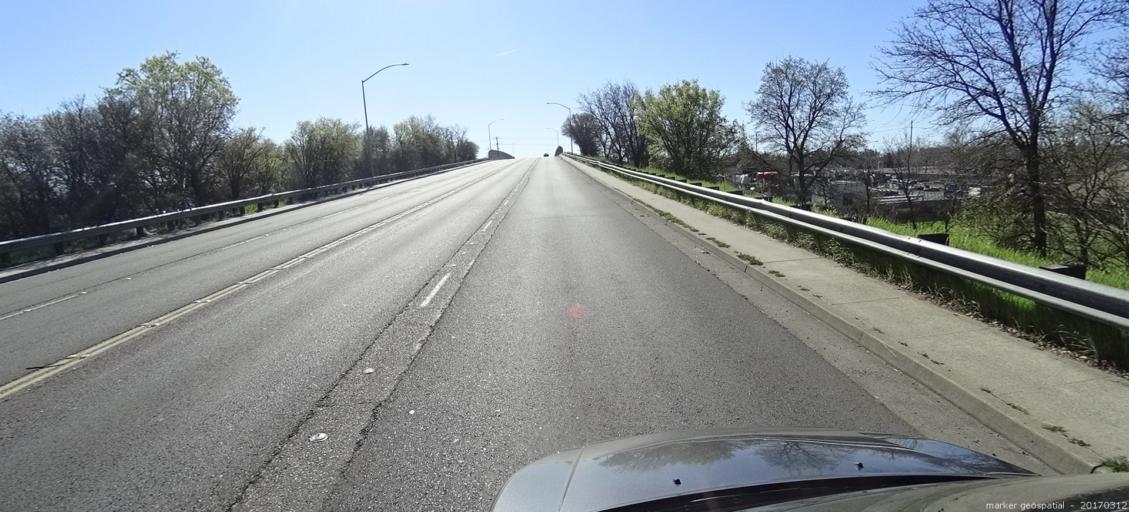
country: US
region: California
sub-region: Sacramento County
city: Arden-Arcade
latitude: 38.6244
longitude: -121.4244
